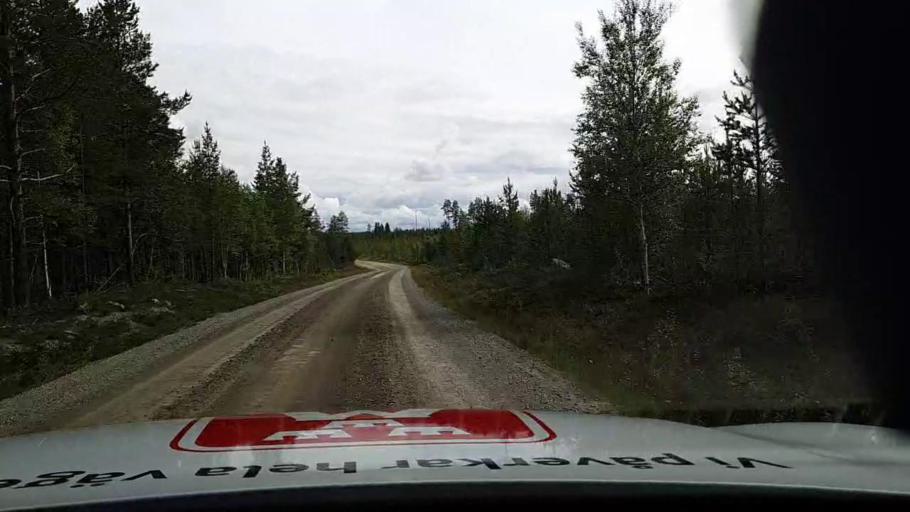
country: SE
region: Jaemtland
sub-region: Are Kommun
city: Jarpen
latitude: 62.5103
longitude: 13.4928
